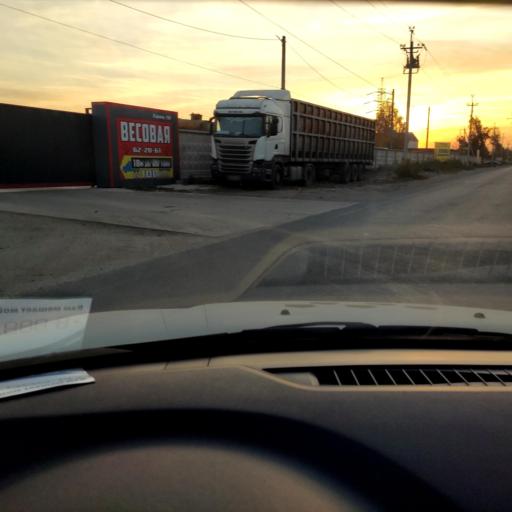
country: RU
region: Samara
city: Tol'yatti
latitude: 53.5286
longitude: 49.4735
